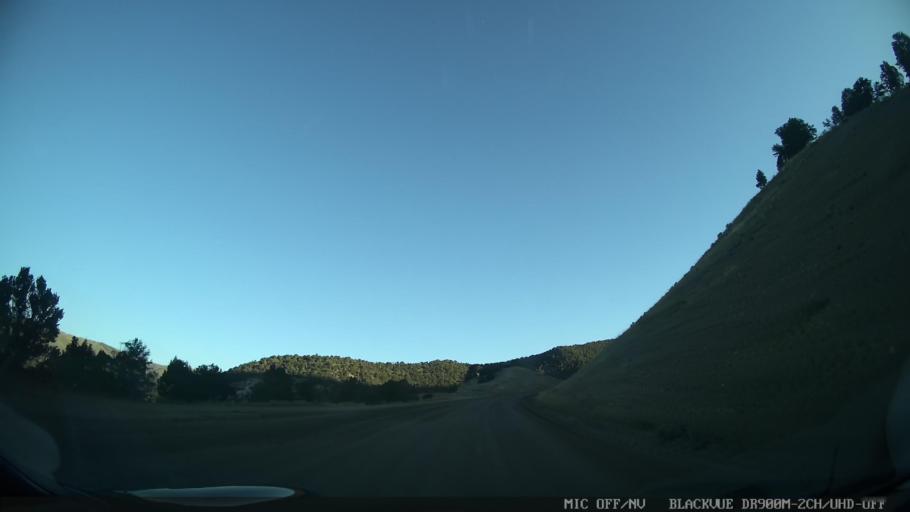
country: US
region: Colorado
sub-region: Grand County
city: Kremmling
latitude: 39.9449
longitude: -106.5290
